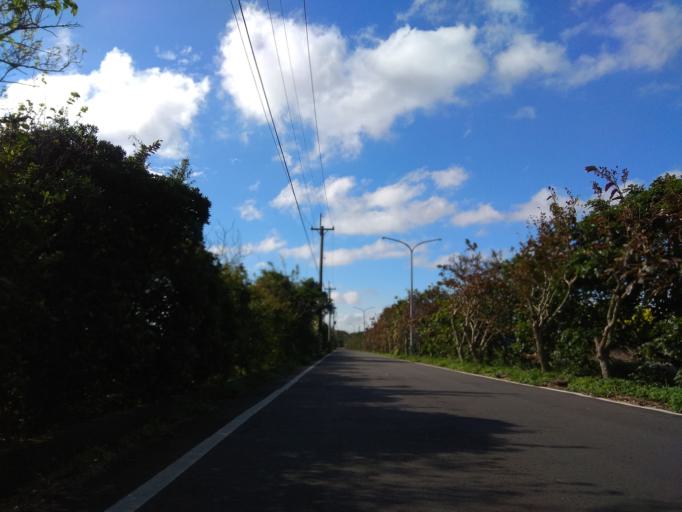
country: TW
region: Taiwan
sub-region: Hsinchu
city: Zhubei
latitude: 24.9737
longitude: 121.0910
